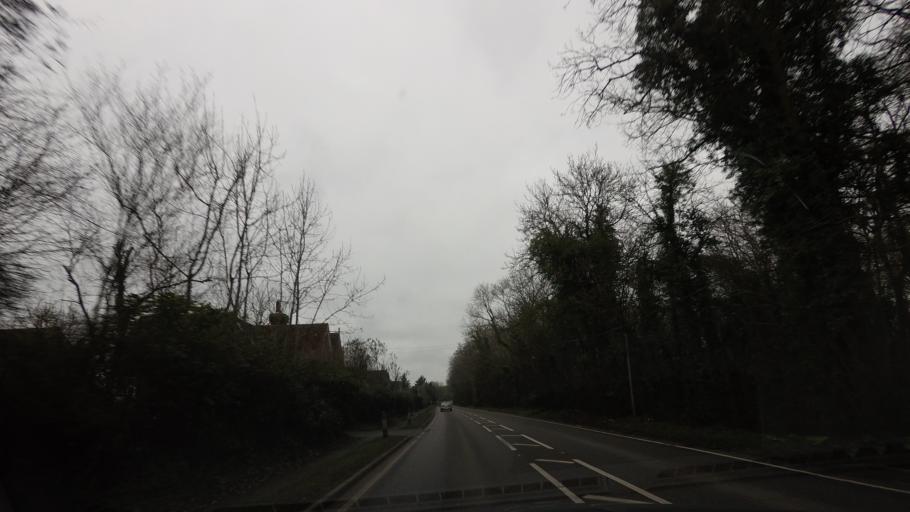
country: GB
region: England
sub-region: Kent
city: Marden
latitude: 51.2149
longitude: 0.5128
